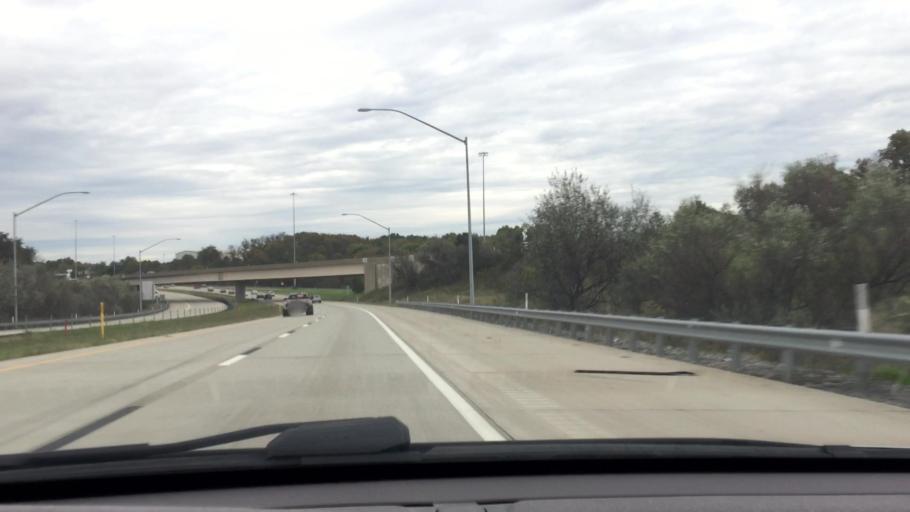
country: US
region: Pennsylvania
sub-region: Allegheny County
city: Carnot-Moon
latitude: 40.5206
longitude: -80.2743
